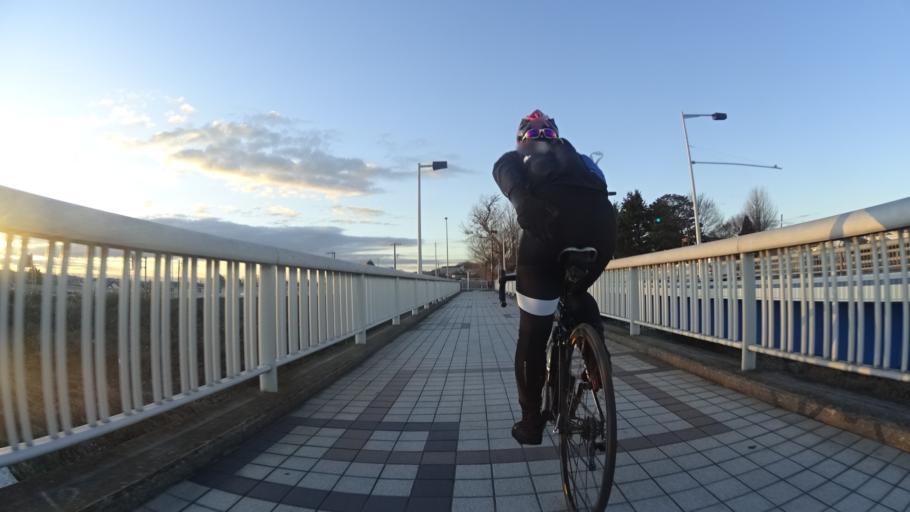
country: JP
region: Kanagawa
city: Zama
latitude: 35.5194
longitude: 139.3662
